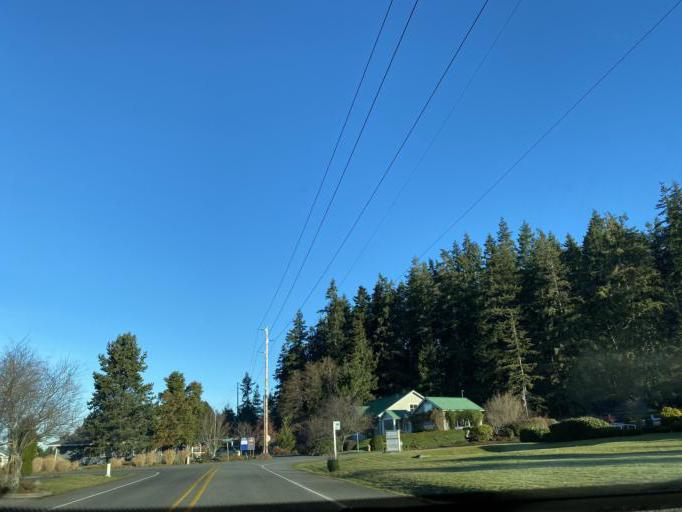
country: US
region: Washington
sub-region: Island County
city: Freeland
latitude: 48.0108
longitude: -122.5243
